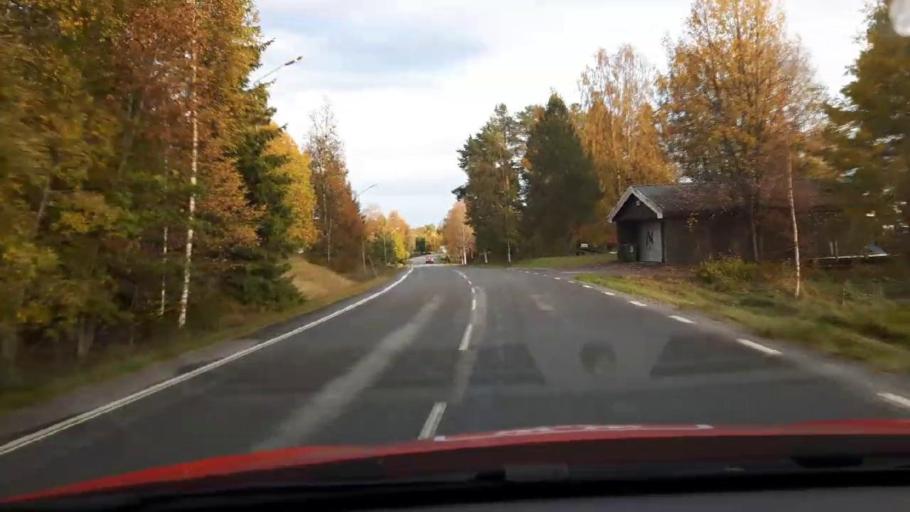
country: SE
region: Jaemtland
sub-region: Krokoms Kommun
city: Krokom
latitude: 63.3455
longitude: 14.5652
